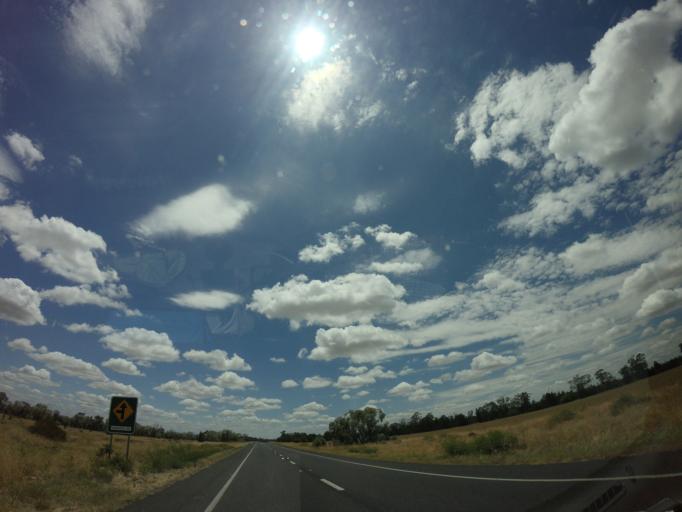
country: AU
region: New South Wales
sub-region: Moree Plains
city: Boggabilla
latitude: -28.8770
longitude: 150.1670
